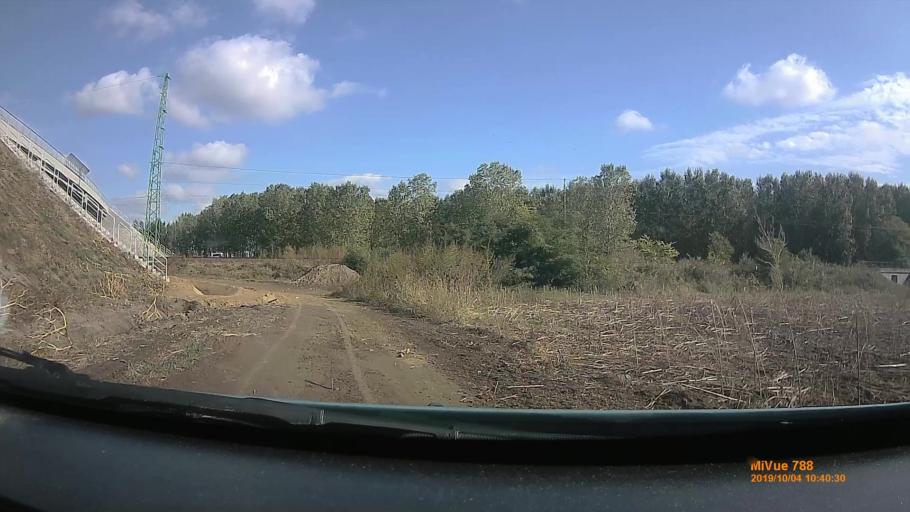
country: HU
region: Szabolcs-Szatmar-Bereg
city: Nyirtelek
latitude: 47.9791
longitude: 21.6639
